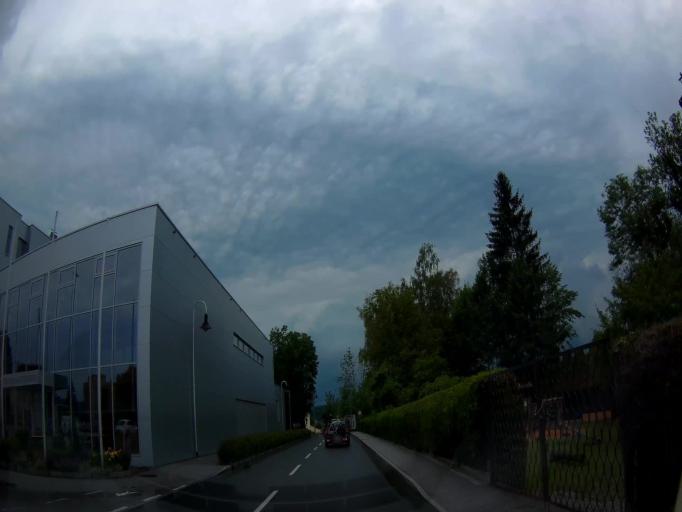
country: AT
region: Salzburg
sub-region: Politischer Bezirk Salzburg-Umgebung
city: Mattsee
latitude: 48.1011
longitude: 13.1498
